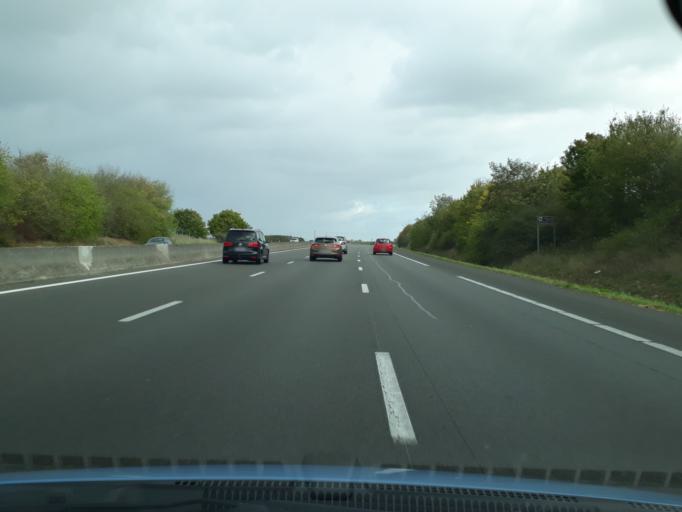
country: FR
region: Centre
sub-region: Departement du Loiret
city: La Chapelle-Saint-Mesmin
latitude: 47.9005
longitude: 1.8188
